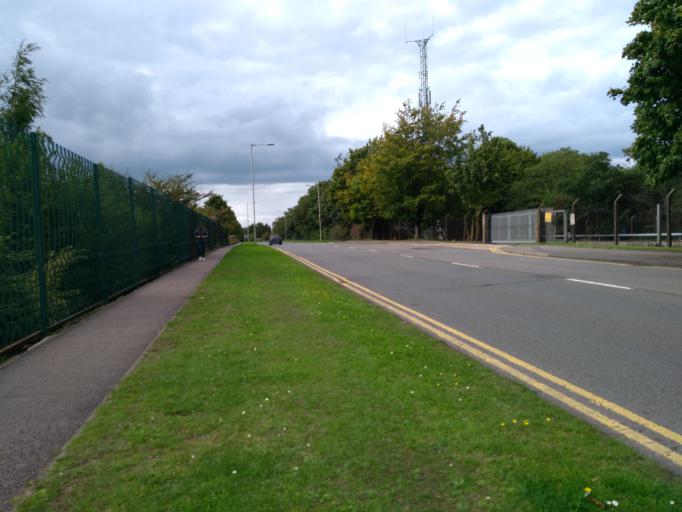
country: GB
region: England
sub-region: Central Bedfordshire
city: Dunstable
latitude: 51.8936
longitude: -0.5147
